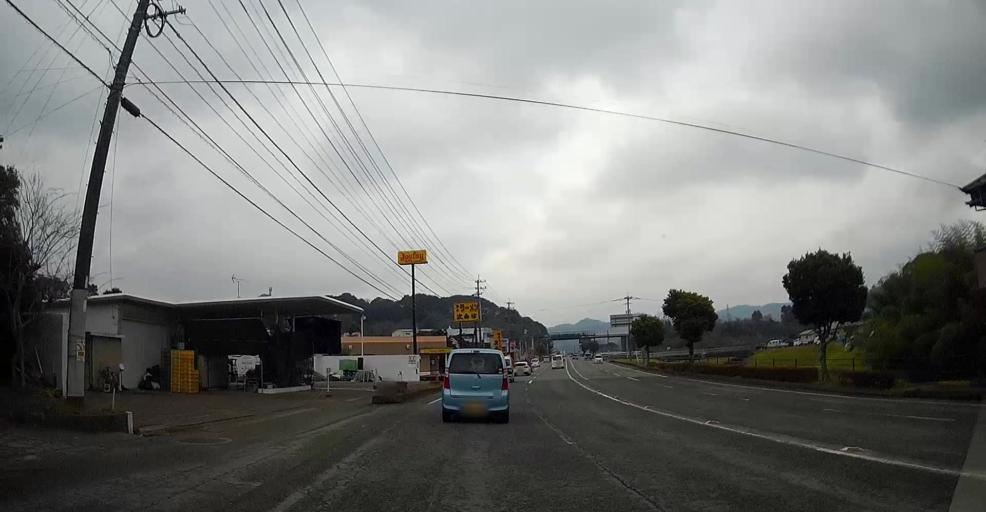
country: JP
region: Kumamoto
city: Matsubase
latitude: 32.6514
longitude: 130.7067
